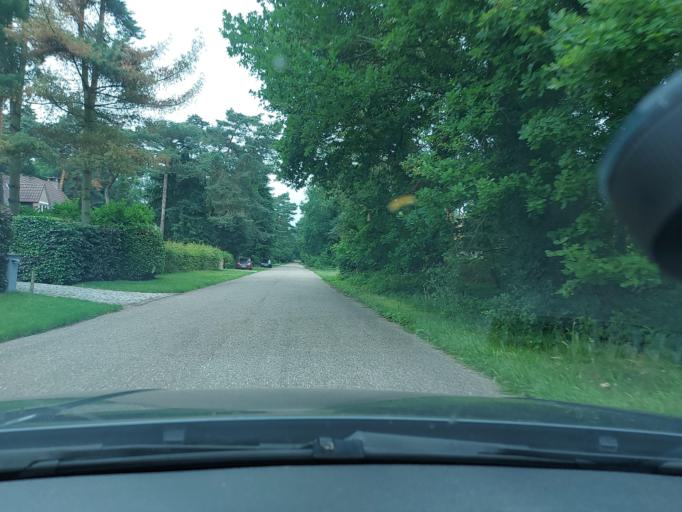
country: BE
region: Flanders
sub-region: Provincie Antwerpen
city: Balen
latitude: 51.1953
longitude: 5.2020
